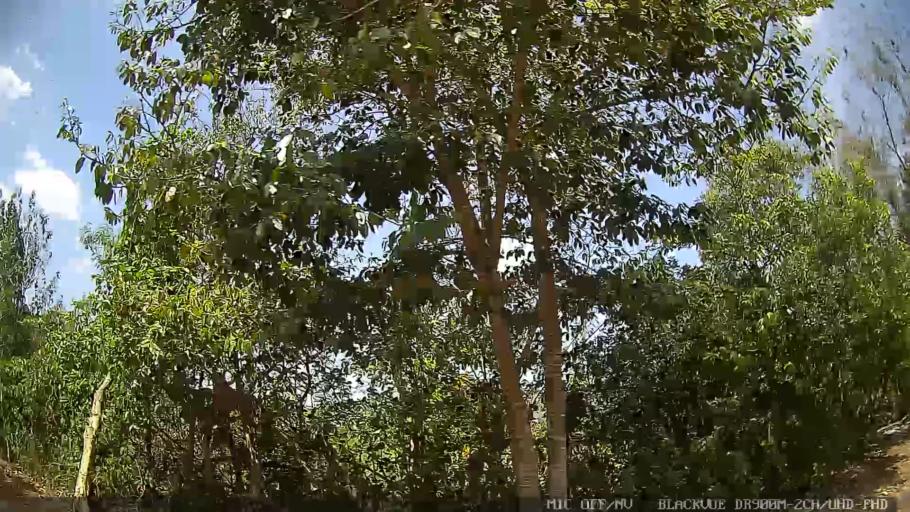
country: BR
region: Sao Paulo
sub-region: Cabreuva
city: Cabreuva
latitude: -23.2617
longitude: -47.0504
